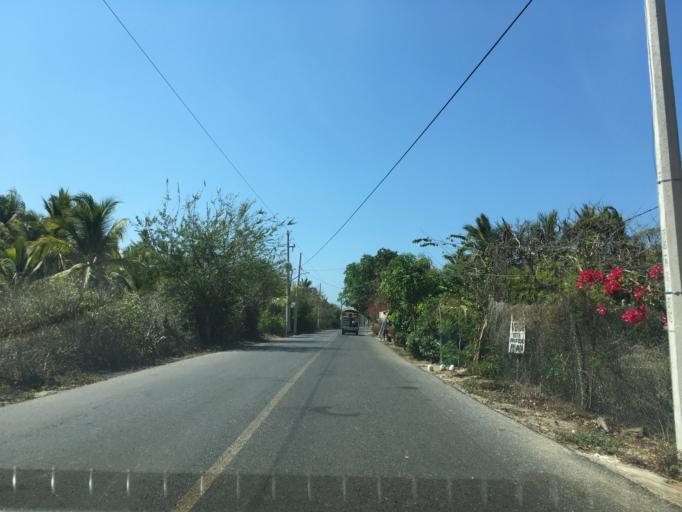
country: MX
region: Guerrero
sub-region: Zihuatanejo de Azueta
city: Los Achotes
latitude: 17.5470
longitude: -101.4386
